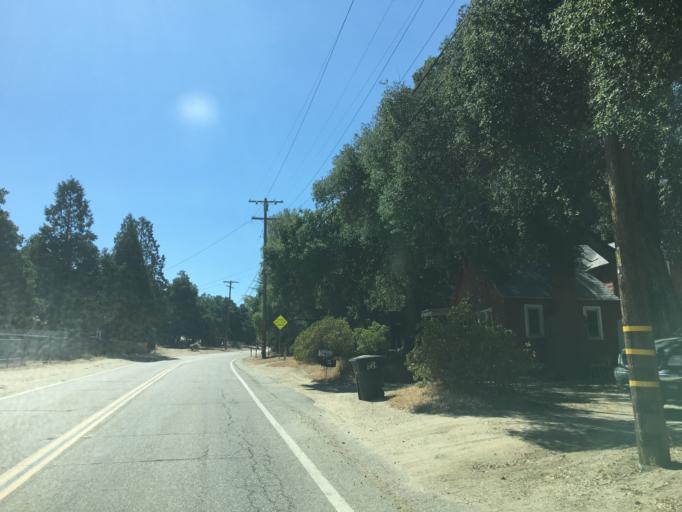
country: US
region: California
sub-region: Los Angeles County
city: Green Valley
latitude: 34.6120
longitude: -118.3973
